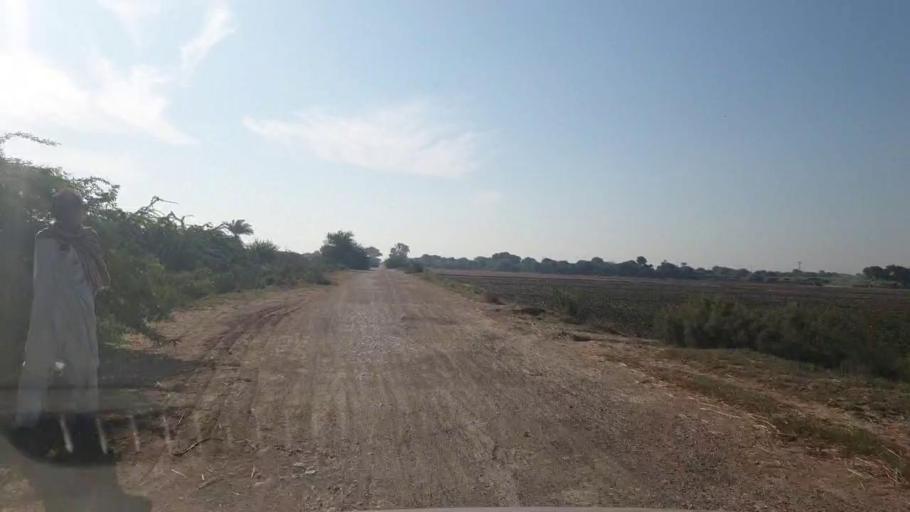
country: PK
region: Sindh
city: Rajo Khanani
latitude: 24.9669
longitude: 68.7953
